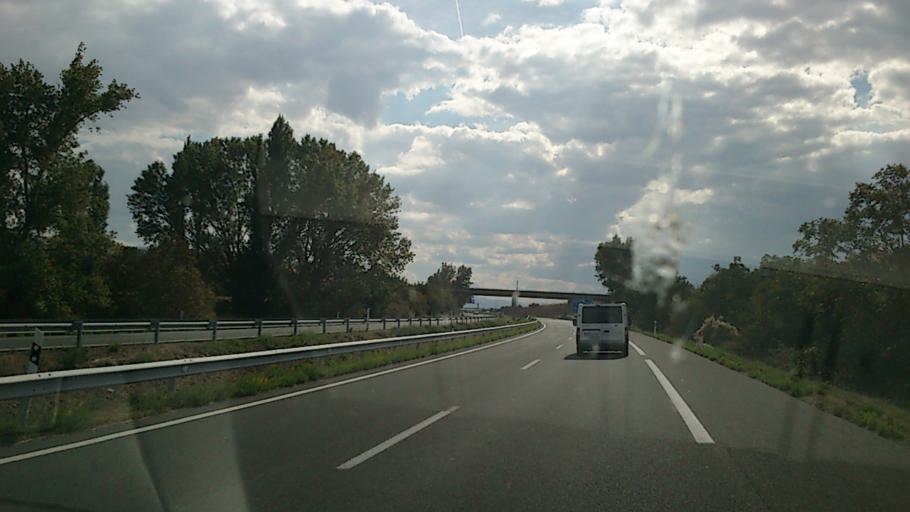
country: ES
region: La Rioja
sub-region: Provincia de La Rioja
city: Anguciana
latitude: 42.5753
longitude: -2.8783
